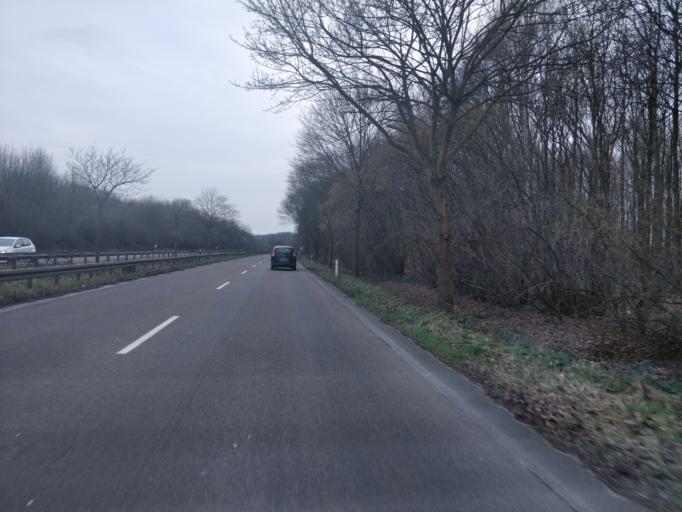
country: DE
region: North Rhine-Westphalia
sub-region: Regierungsbezirk Koln
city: Mengenich
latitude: 50.9572
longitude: 6.8689
